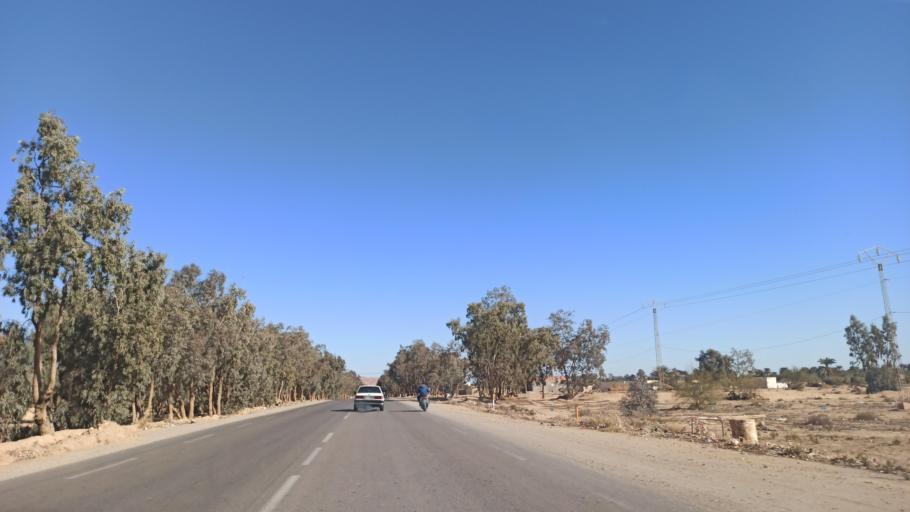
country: TN
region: Gafsa
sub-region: Gafsa Municipality
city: Gafsa
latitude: 34.3952
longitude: 8.7169
